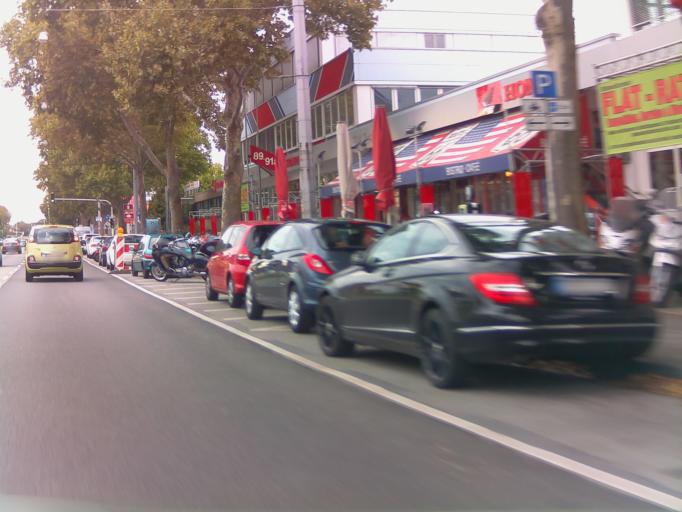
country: DE
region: Rheinland-Pfalz
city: Altrip
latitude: 49.4469
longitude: 8.5080
